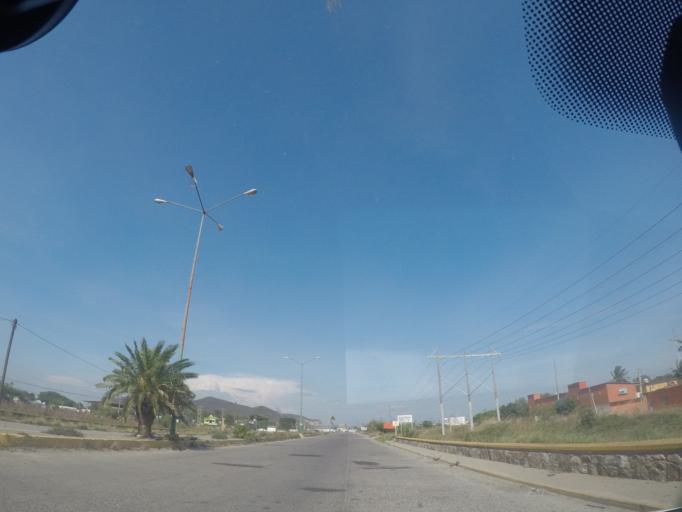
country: MX
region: Oaxaca
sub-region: Salina Cruz
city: Salina Cruz
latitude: 16.2201
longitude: -95.1942
